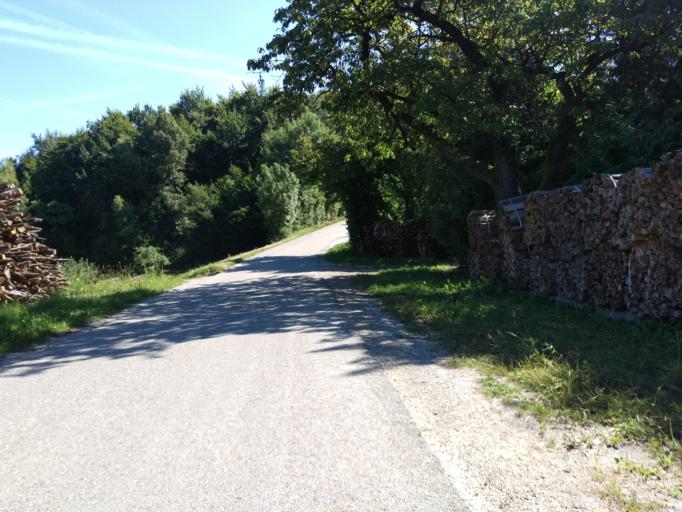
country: AT
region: Styria
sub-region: Politischer Bezirk Graz-Umgebung
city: Edelsgrub
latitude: 47.0606
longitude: 15.5650
